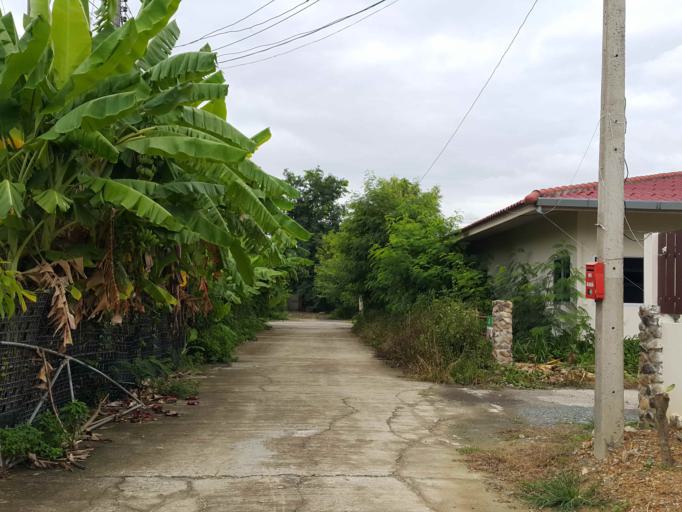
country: TH
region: Chiang Mai
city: San Sai
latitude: 18.8205
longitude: 99.0567
